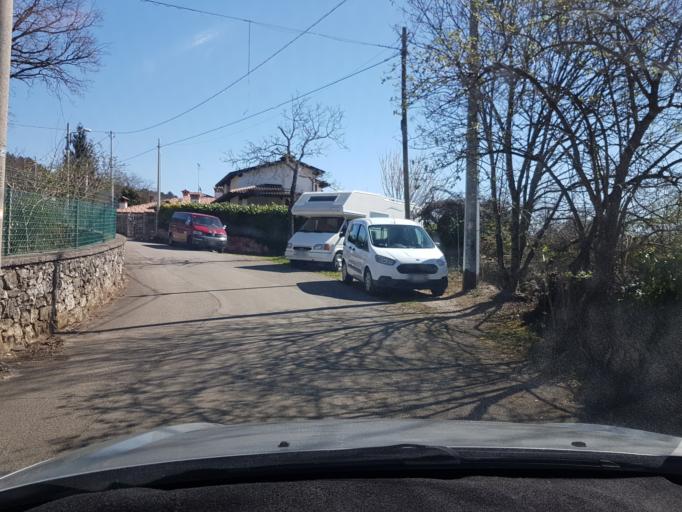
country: IT
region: Friuli Venezia Giulia
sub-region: Provincia di Trieste
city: Santa Croce
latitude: 45.7645
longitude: 13.7045
